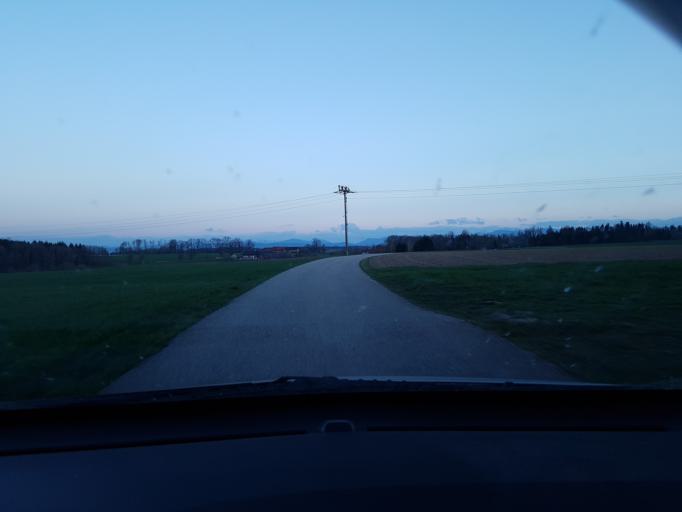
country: AT
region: Upper Austria
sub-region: Politischer Bezirk Linz-Land
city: Ansfelden
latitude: 48.1725
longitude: 14.3209
